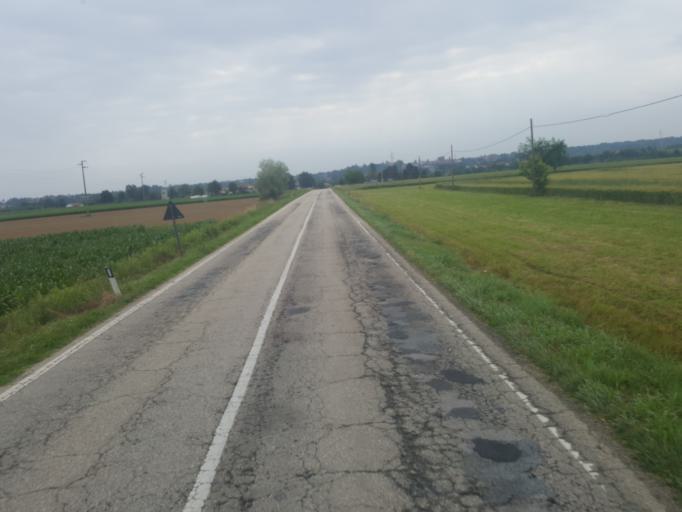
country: IT
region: Piedmont
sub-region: Provincia di Torino
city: Pralormo
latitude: 44.8557
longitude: 7.8666
